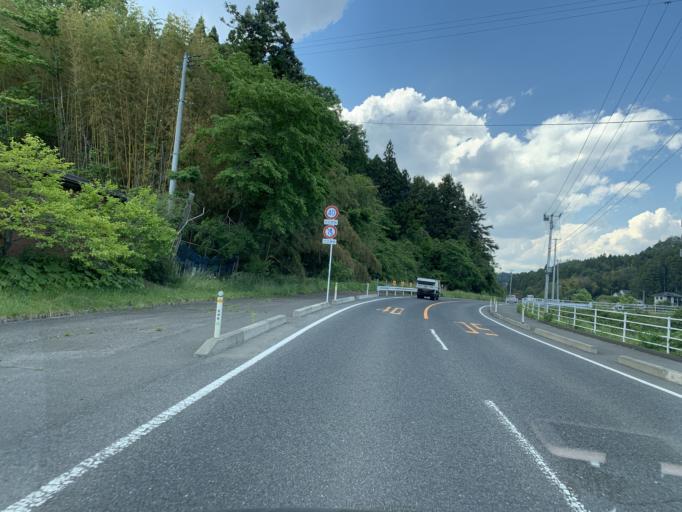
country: JP
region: Miyagi
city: Wakuya
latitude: 38.5517
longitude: 141.1399
